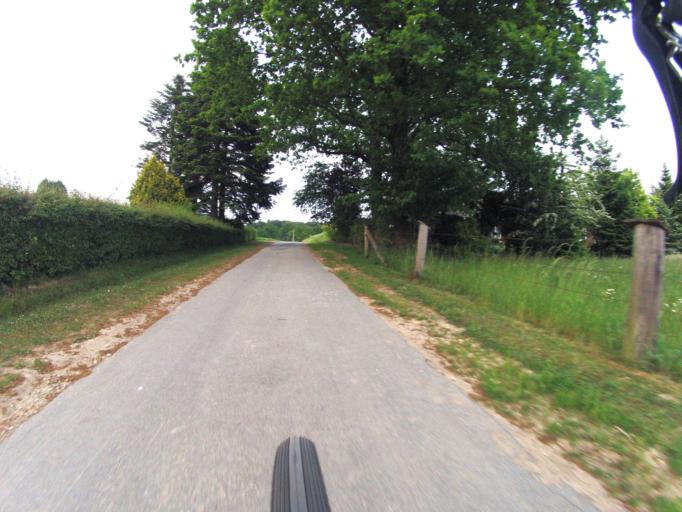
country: DE
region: North Rhine-Westphalia
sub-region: Regierungsbezirk Munster
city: Tecklenburg
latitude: 52.2670
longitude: 7.8064
